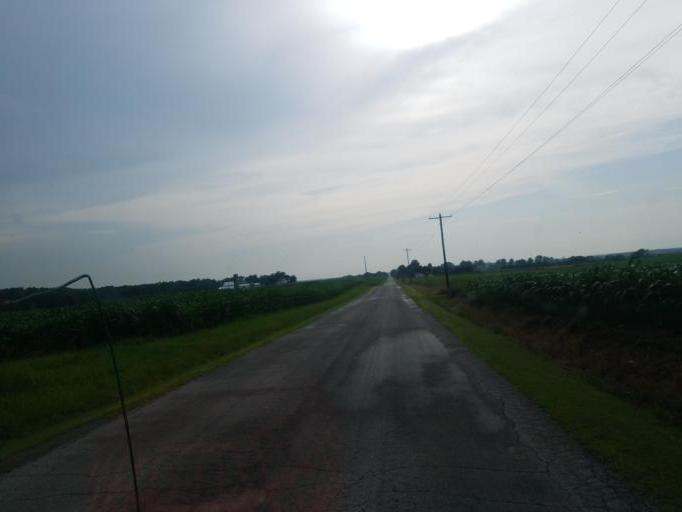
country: US
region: Ohio
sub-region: Wayne County
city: West Salem
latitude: 40.9009
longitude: -82.0828
